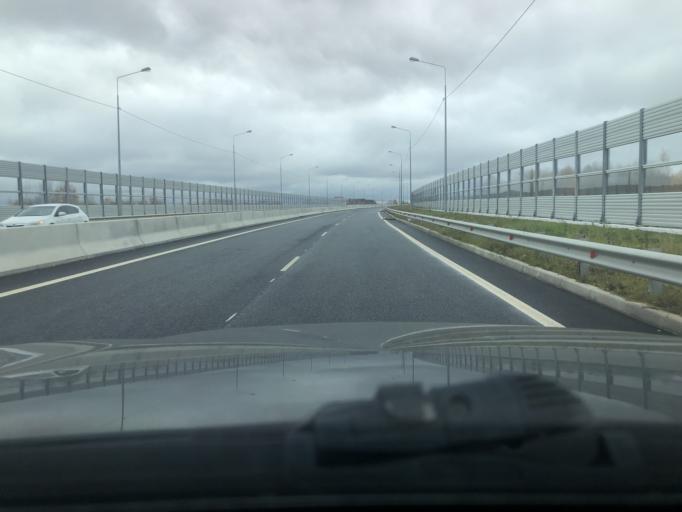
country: RU
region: Moskovskaya
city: Semkhoz
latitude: 56.3163
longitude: 38.0900
